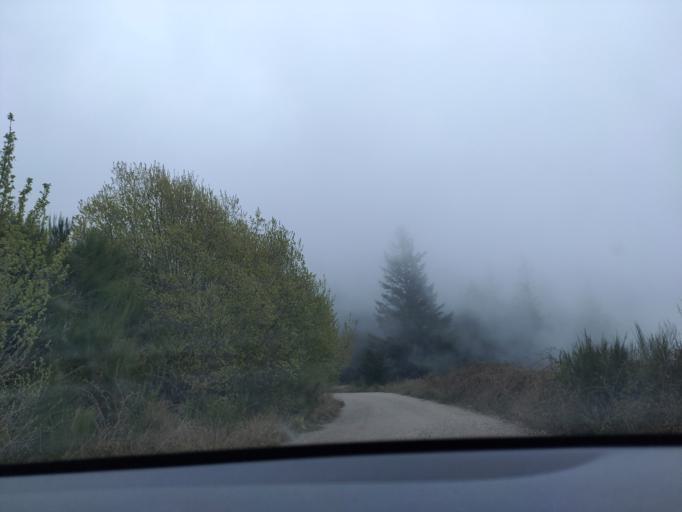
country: ES
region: Catalonia
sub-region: Provincia de Barcelona
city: Fogars de Montclus
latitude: 41.7576
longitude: 2.4552
